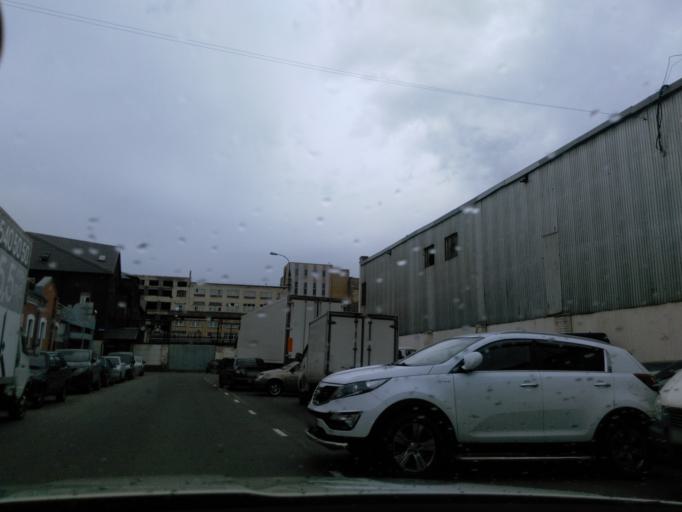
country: RU
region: Moscow
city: Taganskiy
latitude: 55.7298
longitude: 37.6858
